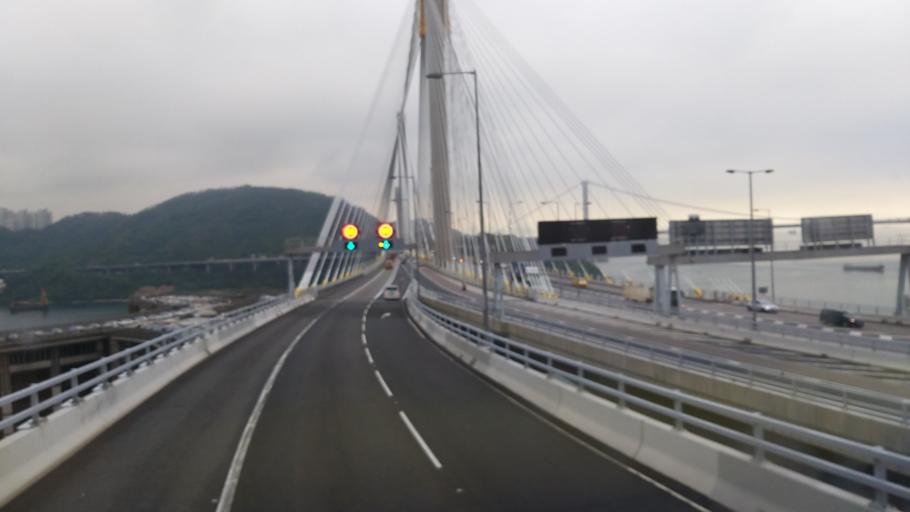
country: HK
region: Tsuen Wan
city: Tsuen Wan
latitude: 22.3695
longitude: 114.0771
